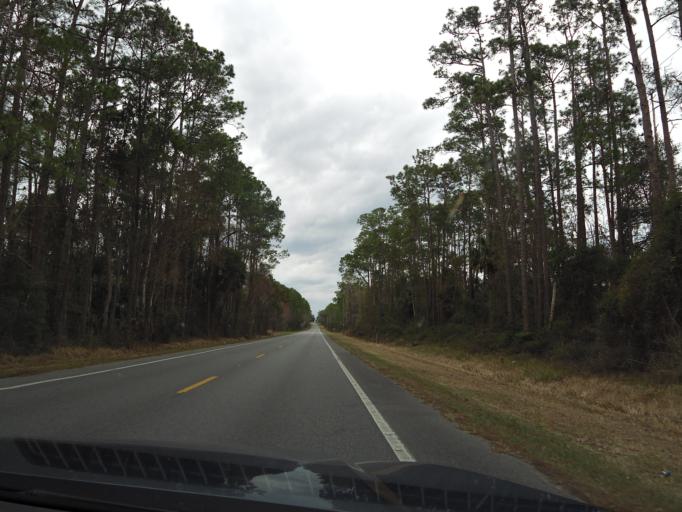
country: US
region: Florida
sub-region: Volusia County
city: Pierson
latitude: 29.2917
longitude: -81.4810
